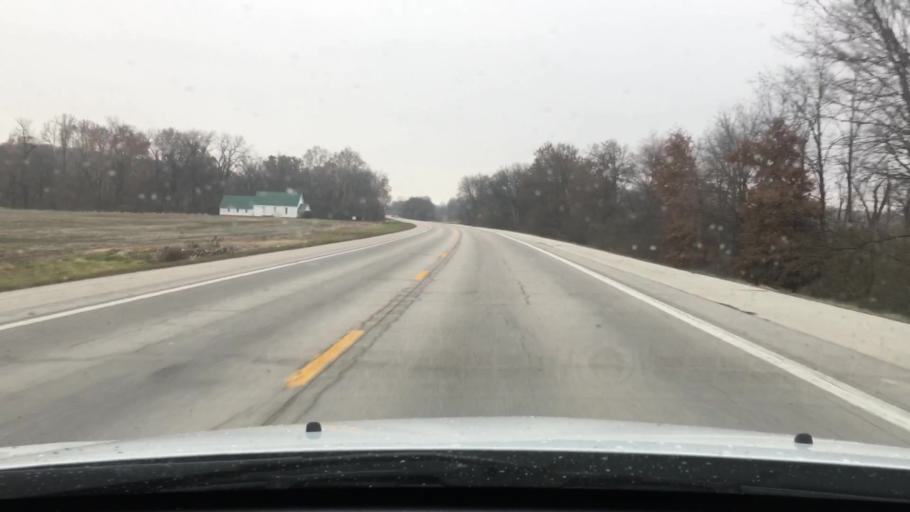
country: US
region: Missouri
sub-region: Pike County
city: Louisiana
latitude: 39.3912
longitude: -91.1163
